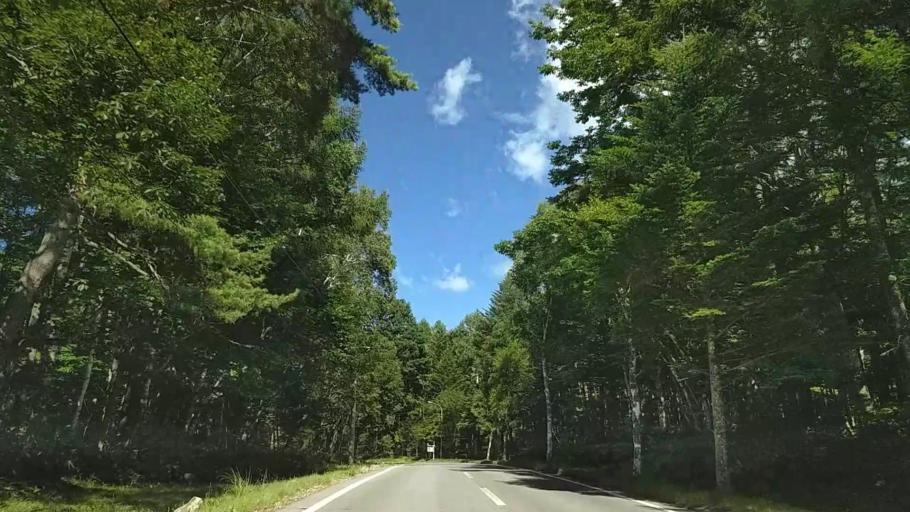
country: JP
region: Nagano
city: Chino
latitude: 36.1234
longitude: 138.2664
